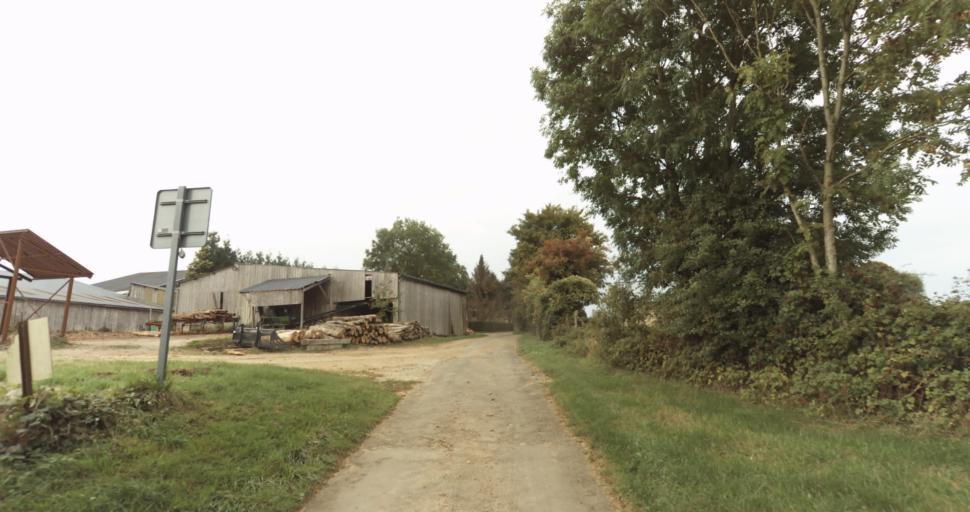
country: FR
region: Lower Normandy
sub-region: Departement de l'Orne
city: Gace
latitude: 48.7646
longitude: 0.3423
